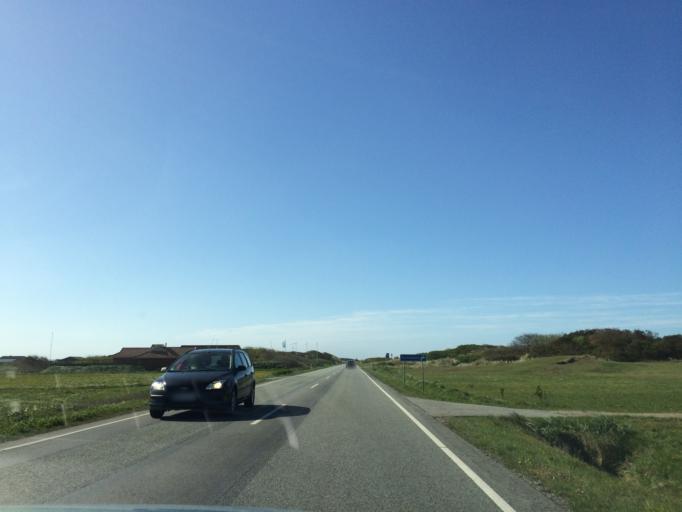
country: DK
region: Central Jutland
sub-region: Ringkobing-Skjern Kommune
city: Hvide Sande
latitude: 55.9632
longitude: 8.1462
